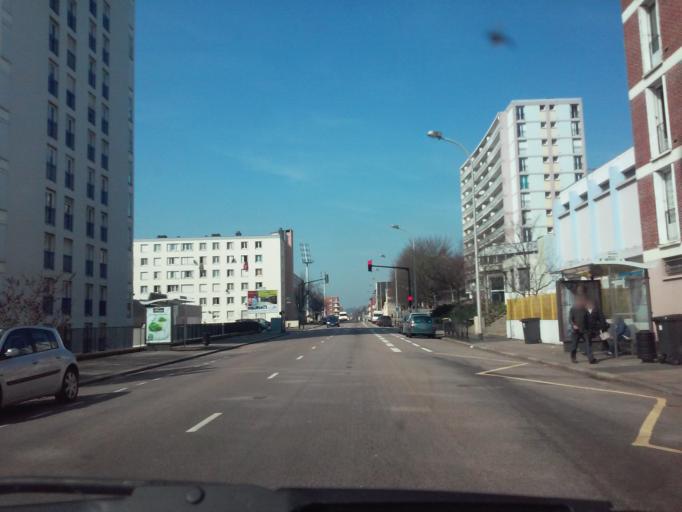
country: FR
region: Haute-Normandie
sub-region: Departement de la Seine-Maritime
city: Harfleur
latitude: 49.5024
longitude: 0.1759
